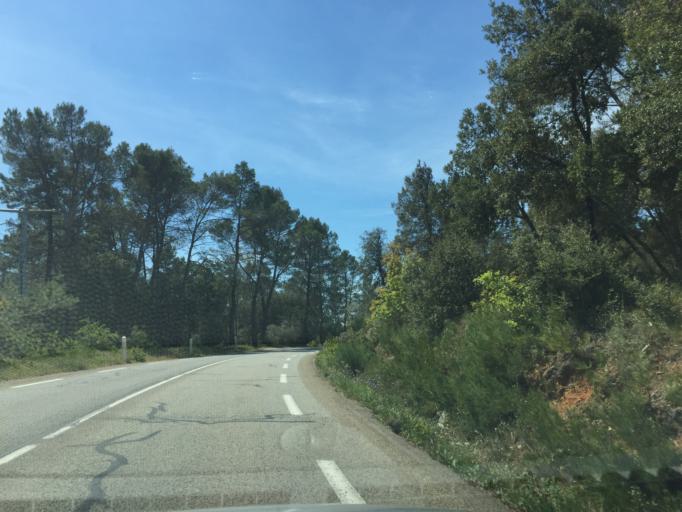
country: FR
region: Provence-Alpes-Cote d'Azur
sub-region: Departement du Var
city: Lorgues
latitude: 43.5112
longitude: 6.3413
